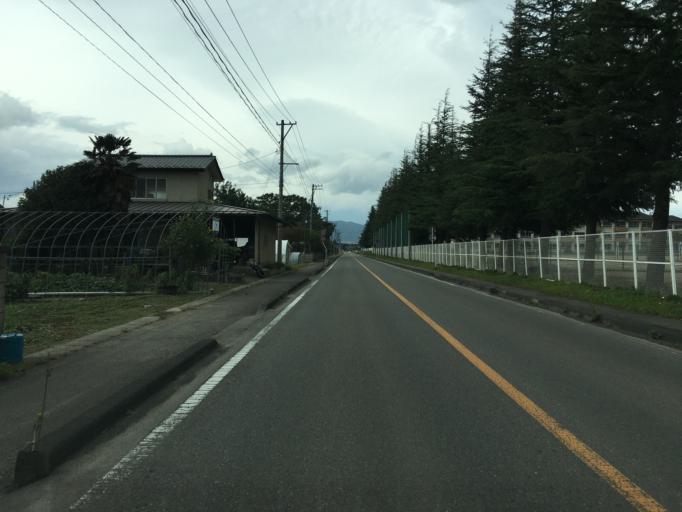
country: JP
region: Fukushima
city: Hobaramachi
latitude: 37.8306
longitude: 140.5574
